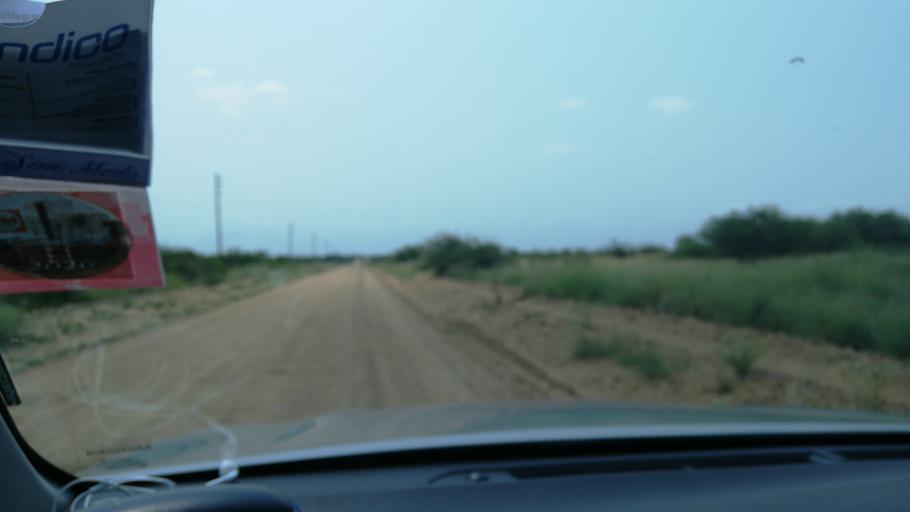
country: MZ
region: Maputo
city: Matola
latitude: -26.0733
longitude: 32.3908
